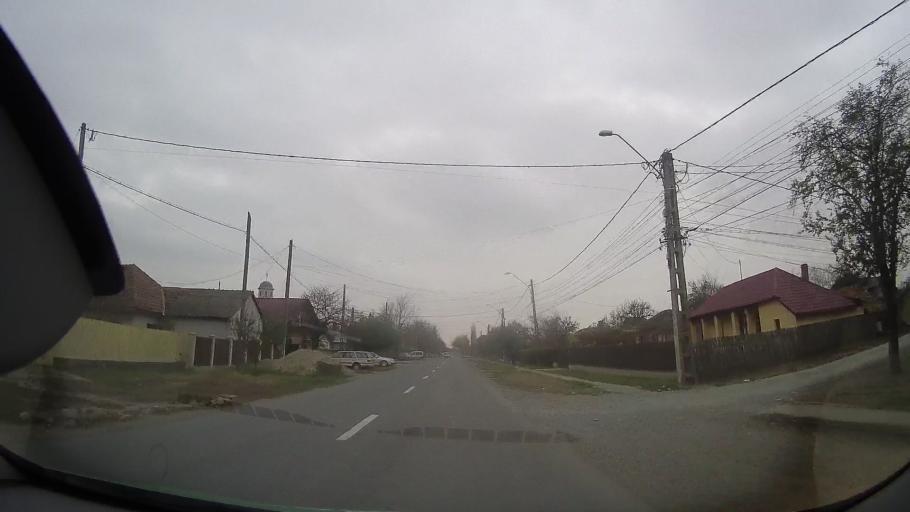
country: RO
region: Ialomita
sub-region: Comuna Manasia
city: Manasia
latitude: 44.7117
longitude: 26.6762
